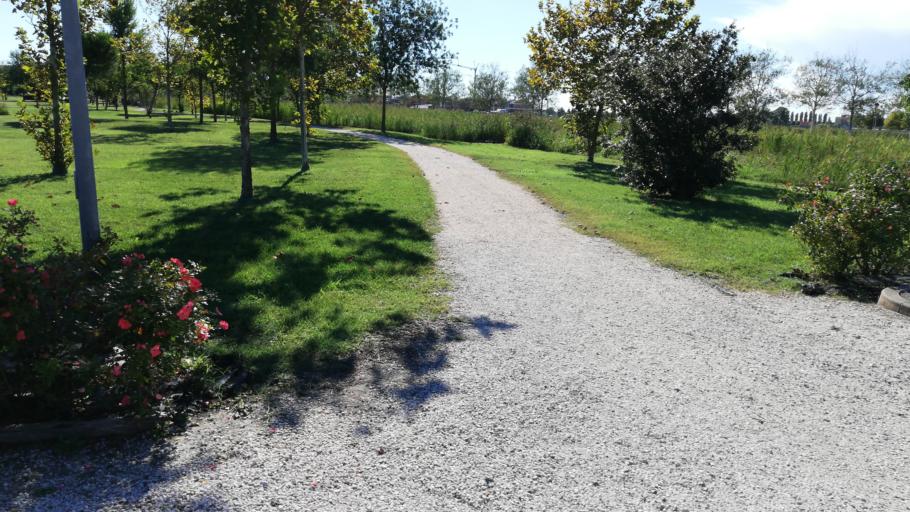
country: IT
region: Veneto
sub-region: Provincia di Venezia
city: Caorle
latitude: 45.5807
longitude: 12.8393
